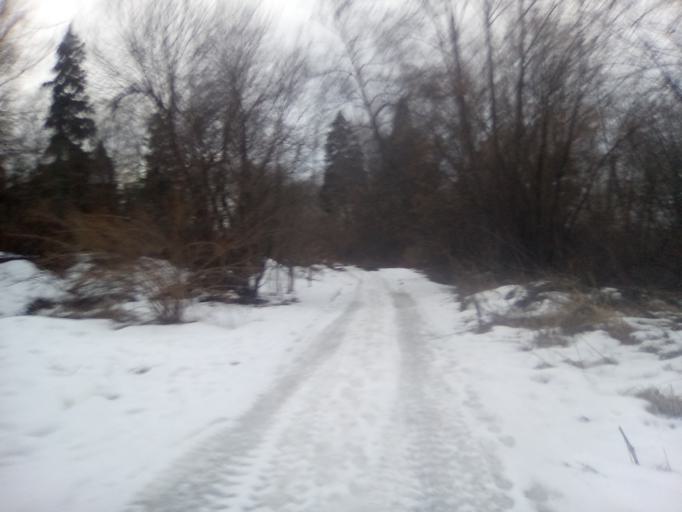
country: RU
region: Moskovskaya
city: Vatutinki
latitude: 55.5134
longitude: 37.3836
